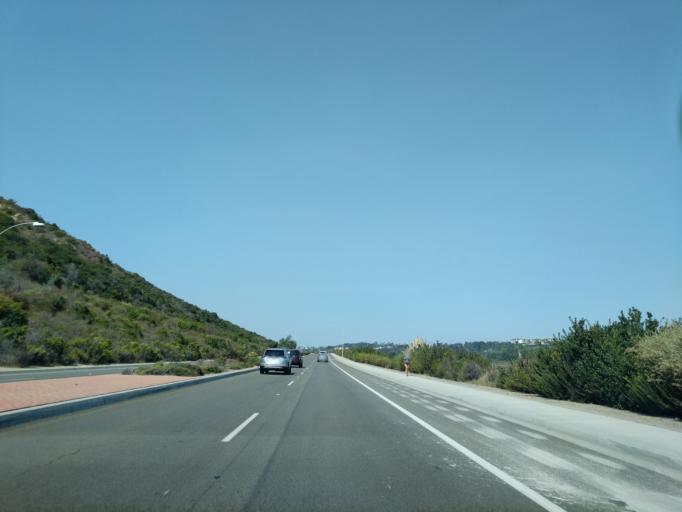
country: US
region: California
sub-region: San Diego County
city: Encinitas
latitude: 33.0860
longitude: -117.2743
